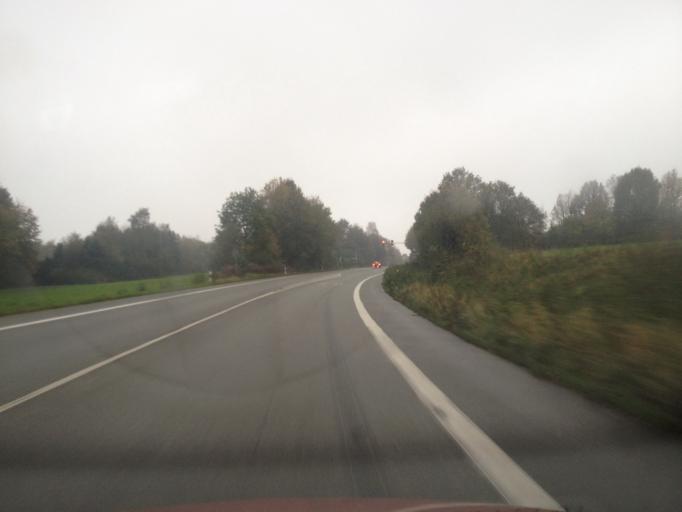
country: DE
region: North Rhine-Westphalia
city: Enger
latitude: 52.0989
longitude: 8.5779
